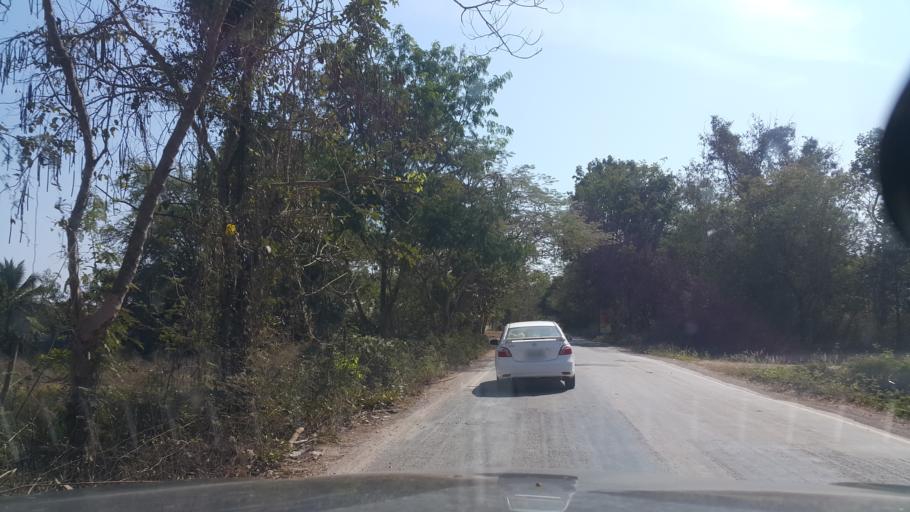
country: TH
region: Changwat Udon Thani
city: Udon Thani
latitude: 17.4942
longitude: 102.7628
